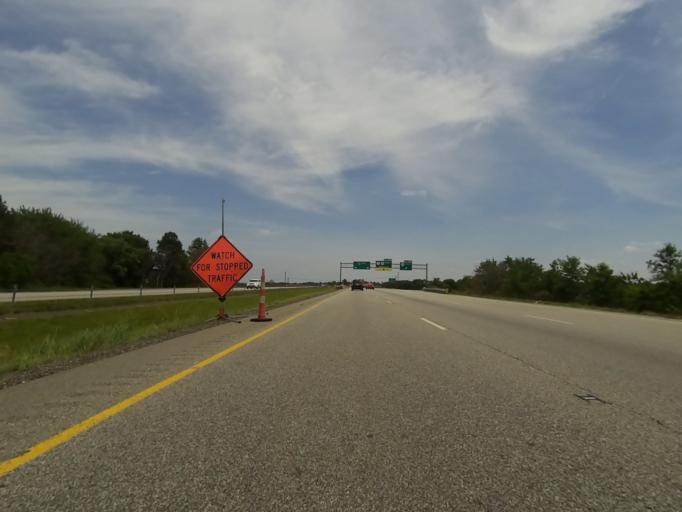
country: US
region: Ohio
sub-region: Portage County
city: Ravenna
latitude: 41.1098
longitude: -81.2464
